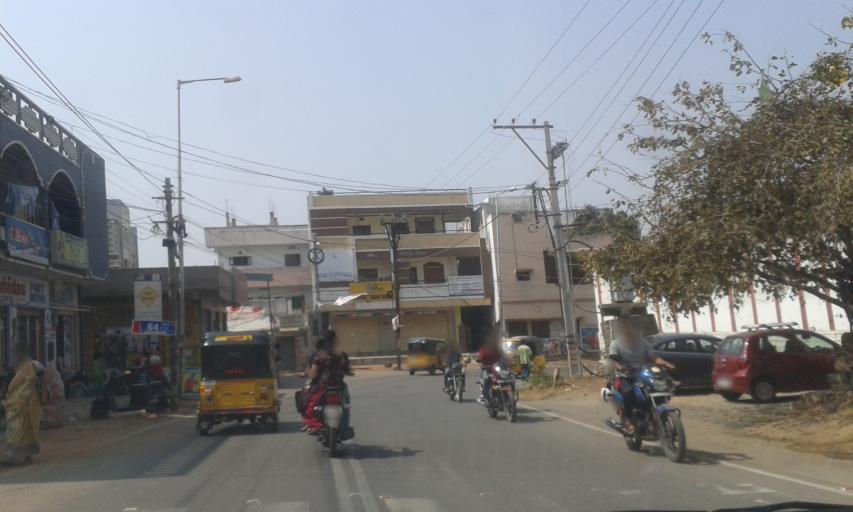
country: IN
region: Telangana
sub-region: Rangareddi
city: Secunderabad
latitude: 17.5037
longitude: 78.5088
